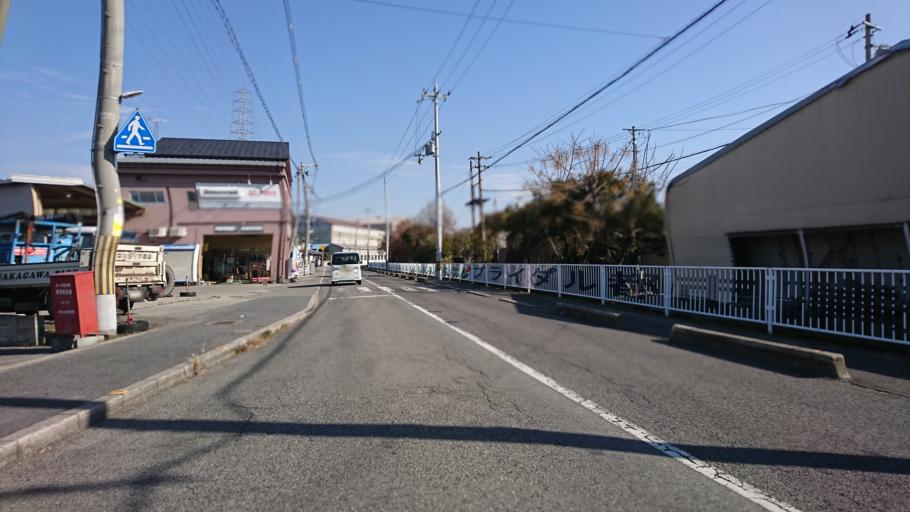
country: JP
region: Hyogo
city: Kakogawacho-honmachi
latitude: 34.7761
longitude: 134.8130
